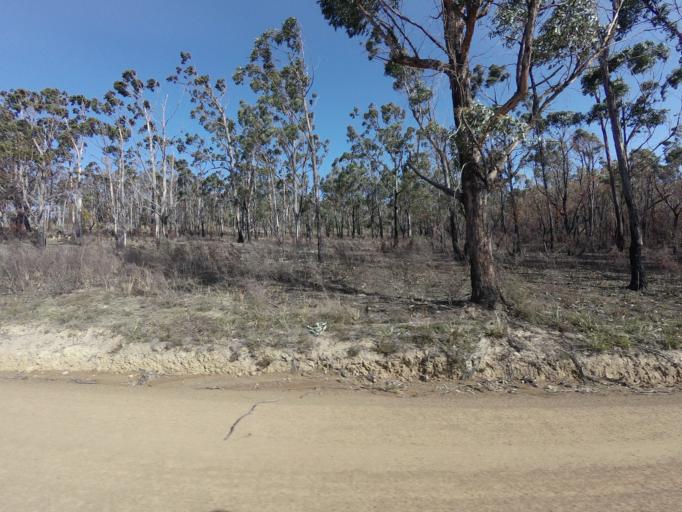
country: AU
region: Tasmania
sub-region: Kingborough
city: Kettering
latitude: -43.0819
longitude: 147.2639
